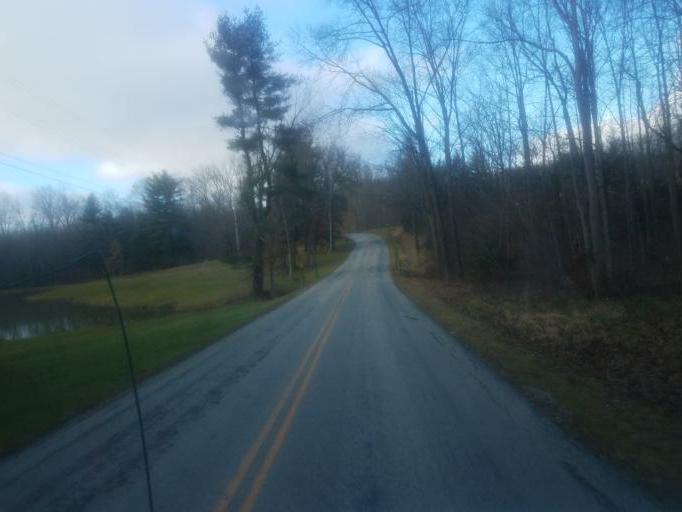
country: US
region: Ohio
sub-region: Sandusky County
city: Bellville
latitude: 40.6006
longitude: -82.3763
